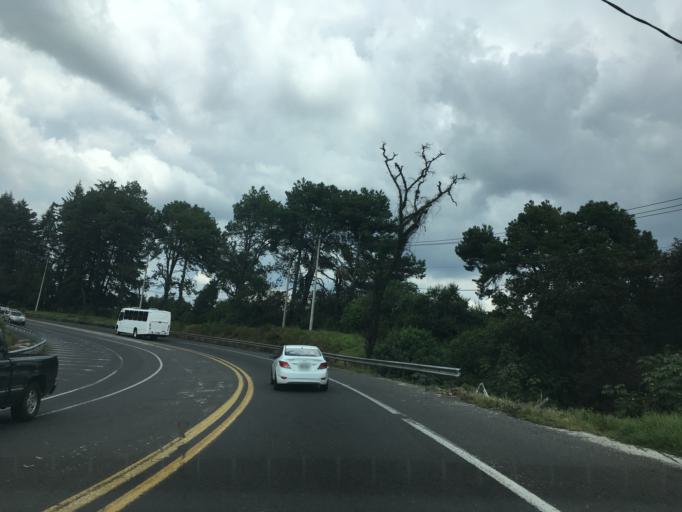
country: MX
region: Michoacan
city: Capacuaro
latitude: 19.4821
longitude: -102.0689
